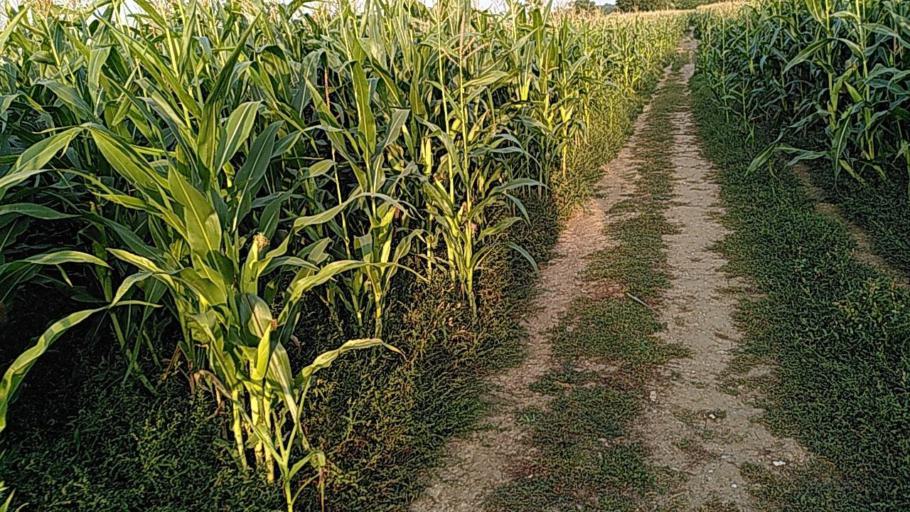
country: GB
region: England
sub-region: Oxfordshire
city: Sonning Common
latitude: 51.4922
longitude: -0.9505
